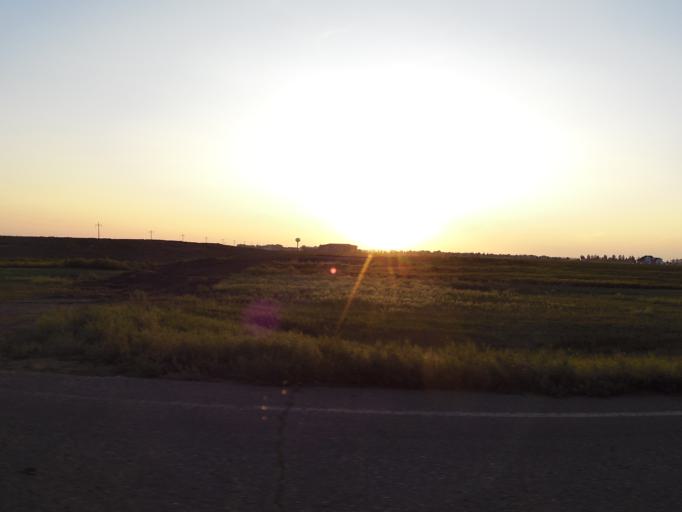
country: US
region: North Dakota
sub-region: Grand Forks County
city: Grand Forks
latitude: 47.8616
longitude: -97.0453
